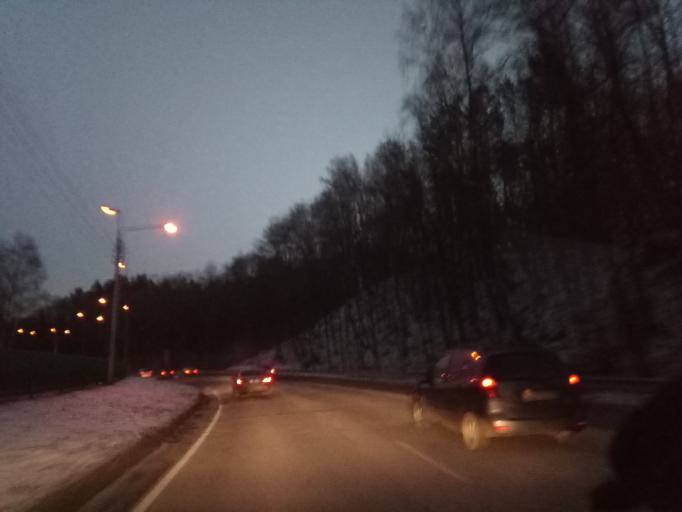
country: LT
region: Vilnius County
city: Lazdynai
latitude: 54.6390
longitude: 25.1879
